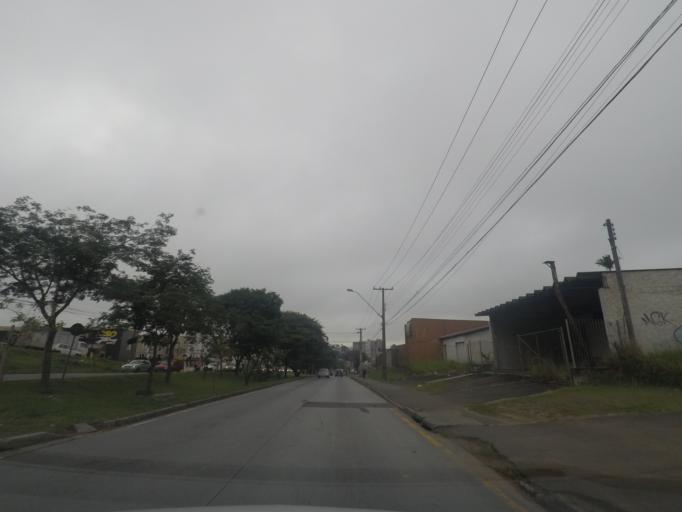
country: BR
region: Parana
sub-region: Pinhais
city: Pinhais
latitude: -25.3799
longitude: -49.2197
